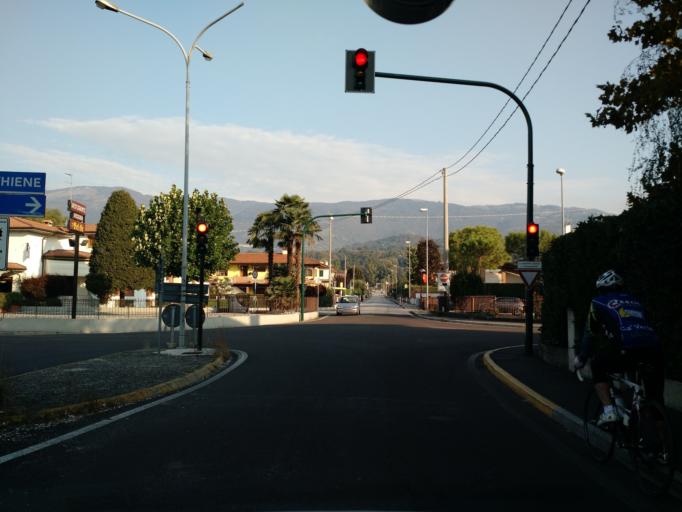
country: IT
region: Veneto
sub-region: Provincia di Vicenza
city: Fara Vicentino
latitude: 45.7370
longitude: 11.5391
